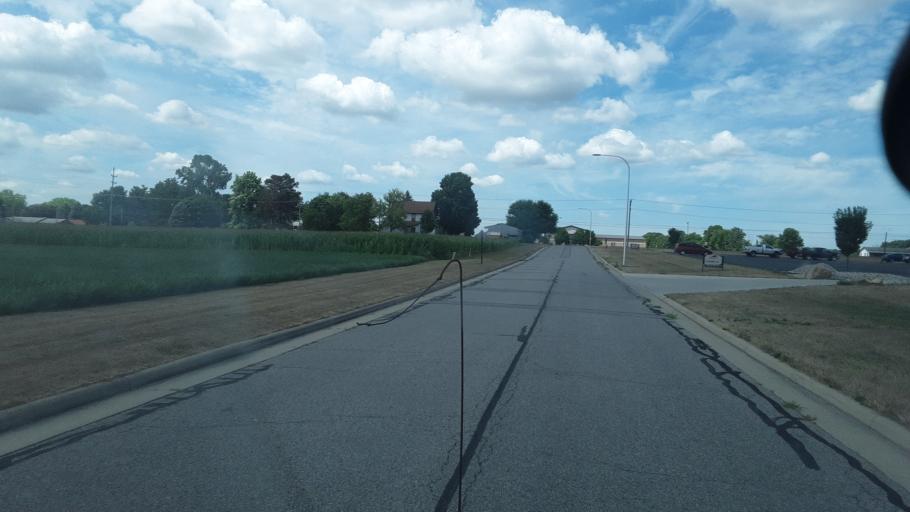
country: US
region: Ohio
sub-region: Defiance County
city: Hicksville
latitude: 41.3070
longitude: -84.7642
